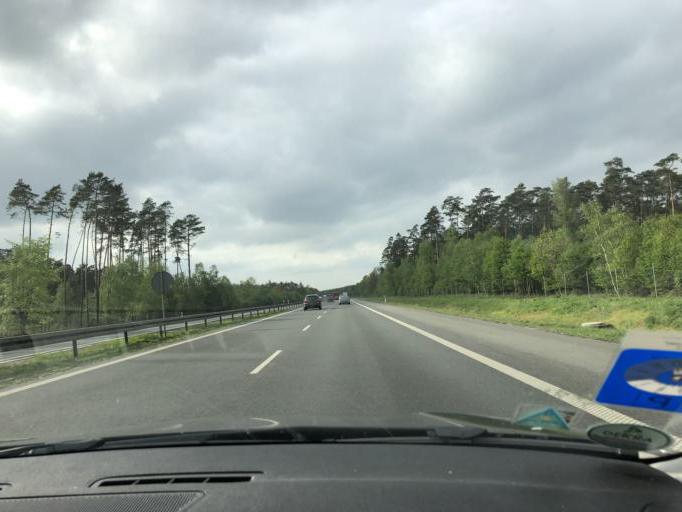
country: PL
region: Opole Voivodeship
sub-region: Powiat opolski
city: Proszkow
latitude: 50.5396
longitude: 17.9008
